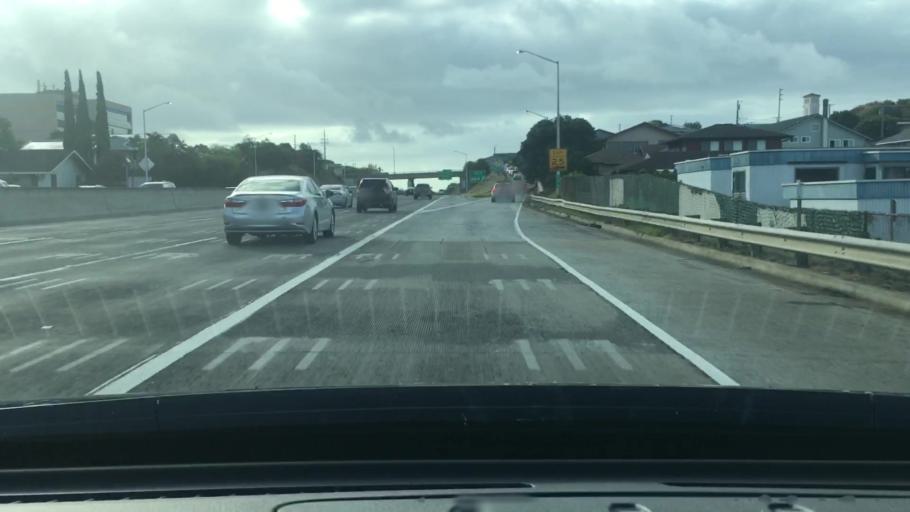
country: US
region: Hawaii
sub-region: Honolulu County
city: Honolulu
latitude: 21.2808
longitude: -157.8015
